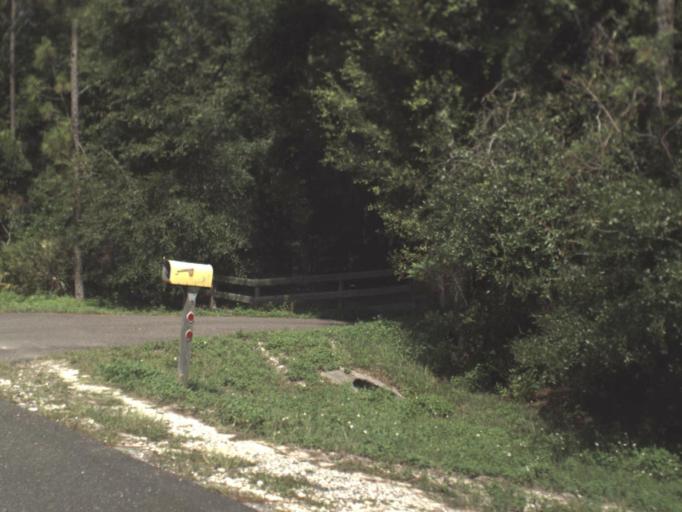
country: US
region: Florida
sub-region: Levy County
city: East Bronson
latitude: 29.4960
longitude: -82.5834
